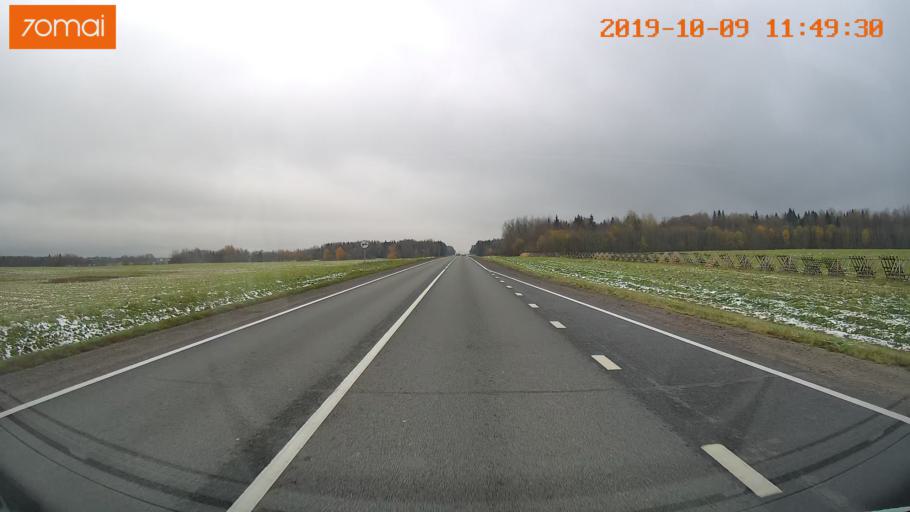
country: RU
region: Vologda
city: Gryazovets
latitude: 58.8179
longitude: 40.2307
